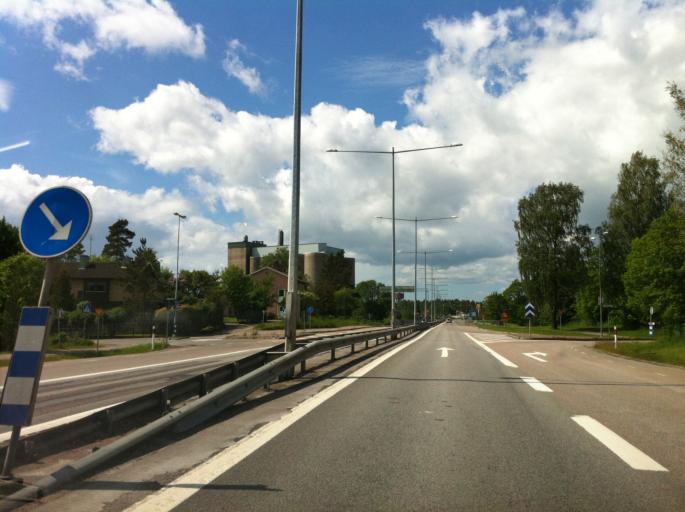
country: SE
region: Vaermland
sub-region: Saffle Kommun
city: Saeffle
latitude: 59.1377
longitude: 12.9297
